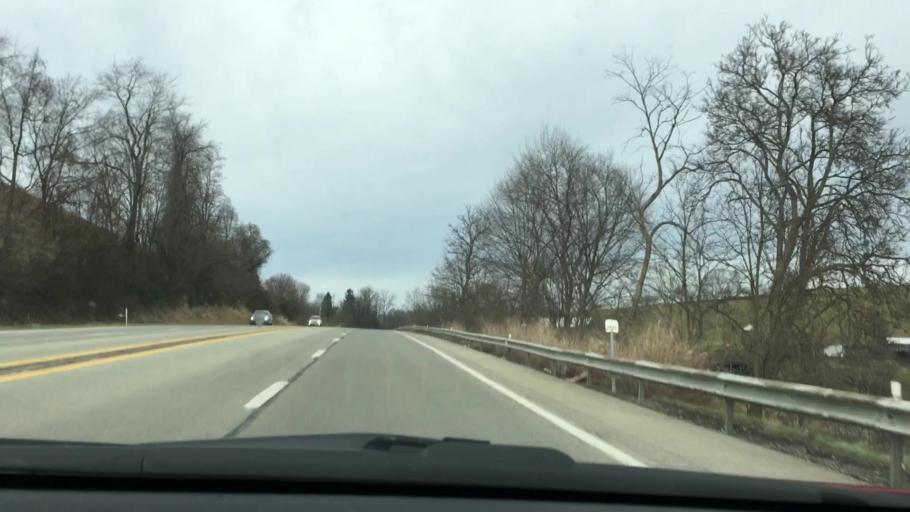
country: US
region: Pennsylvania
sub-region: Fayette County
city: Perryopolis
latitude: 40.0426
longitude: -79.7720
